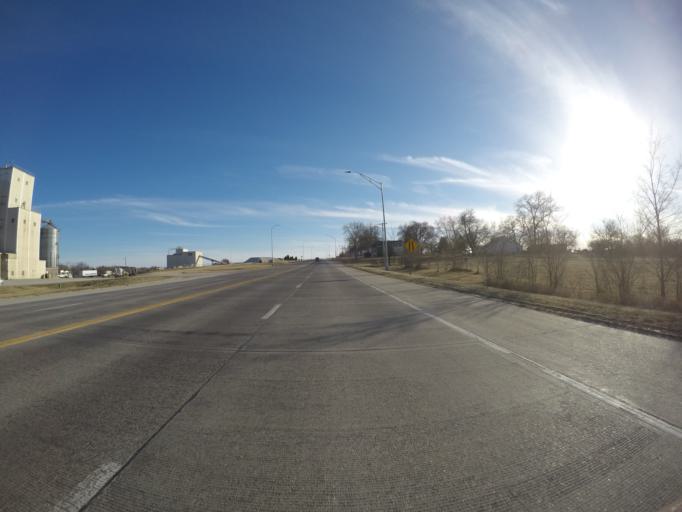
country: US
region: Nebraska
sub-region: Gage County
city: Beatrice
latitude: 40.2425
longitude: -96.7463
